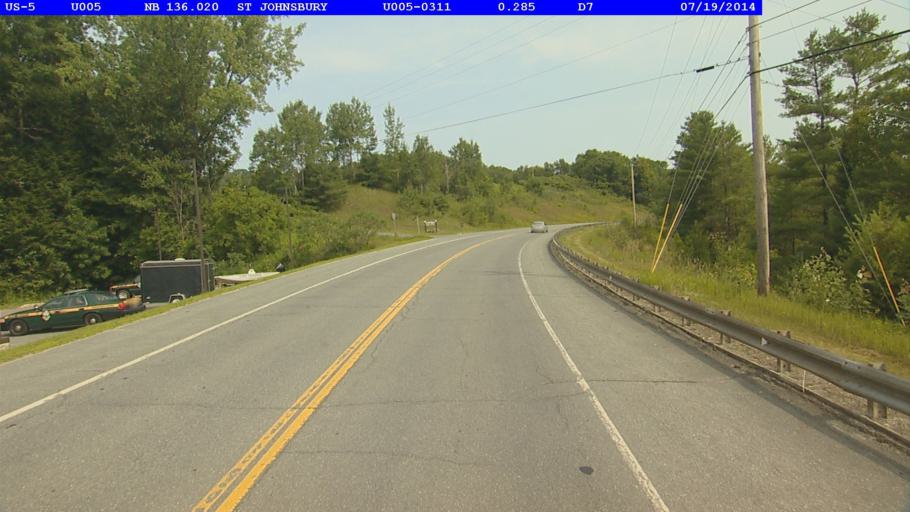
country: US
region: Vermont
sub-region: Caledonia County
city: Saint Johnsbury
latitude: 44.3986
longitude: -72.0252
